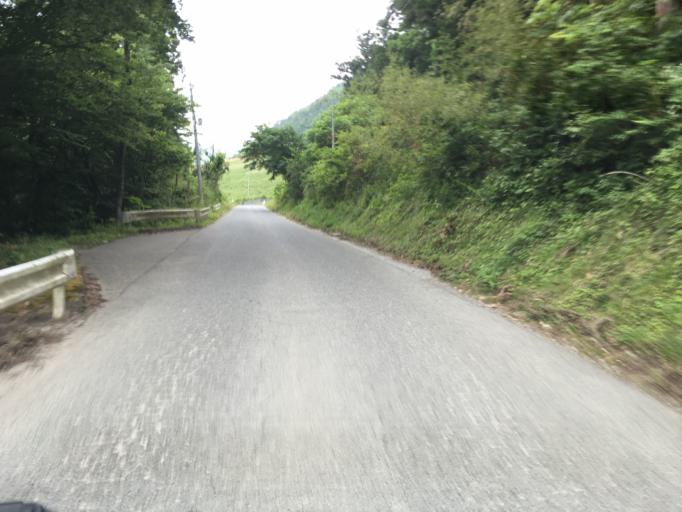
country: JP
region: Miyagi
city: Marumori
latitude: 37.7823
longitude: 140.7953
